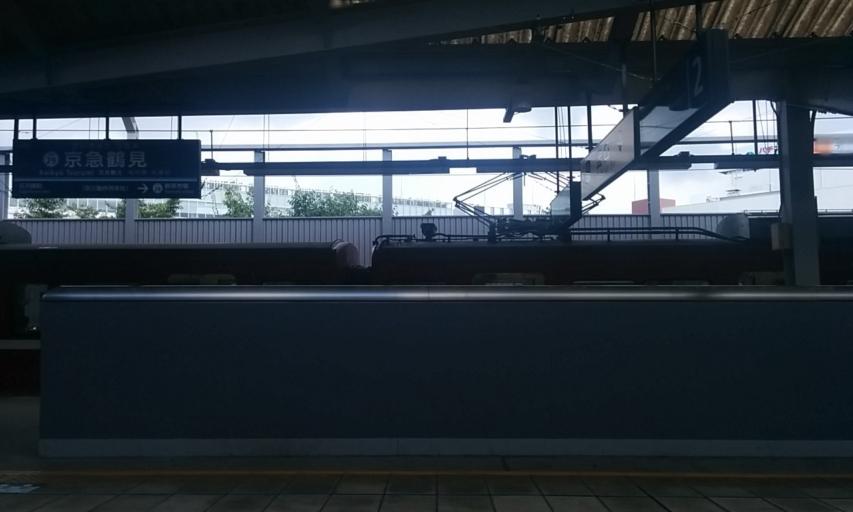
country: JP
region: Kanagawa
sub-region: Kawasaki-shi
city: Kawasaki
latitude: 35.5075
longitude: 139.6781
